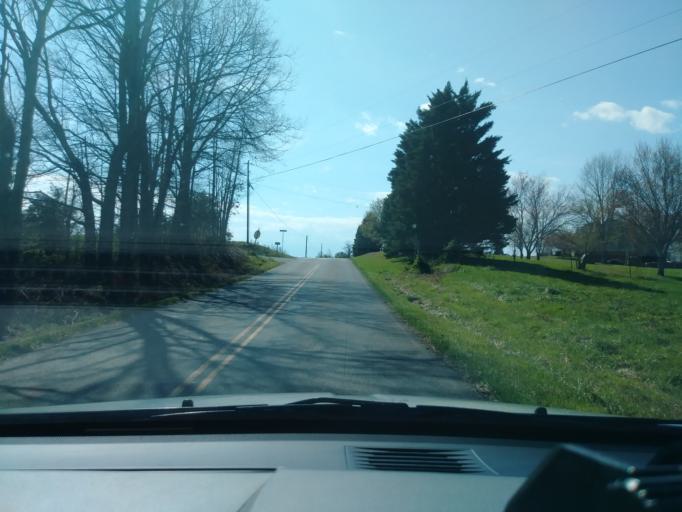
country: US
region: Tennessee
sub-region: Greene County
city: Greeneville
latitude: 36.0678
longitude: -82.7867
